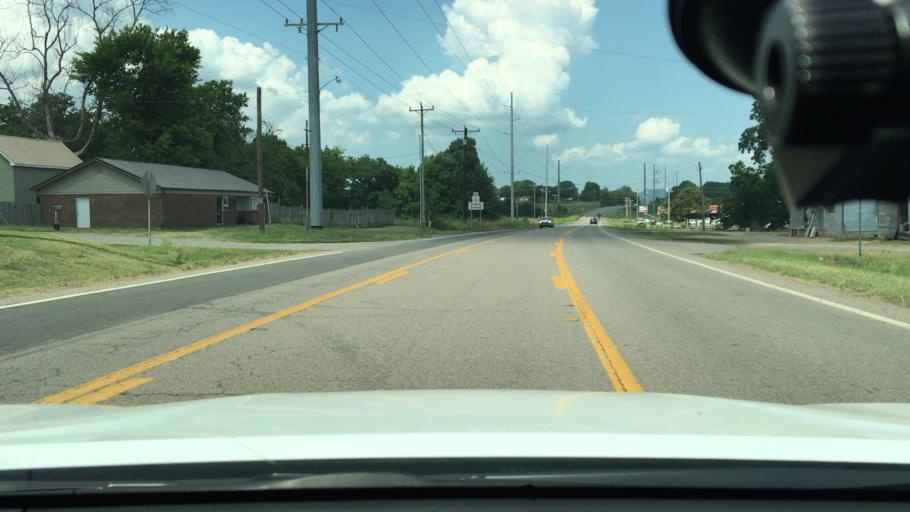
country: US
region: Arkansas
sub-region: Logan County
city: Paris
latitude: 35.2936
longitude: -93.6386
